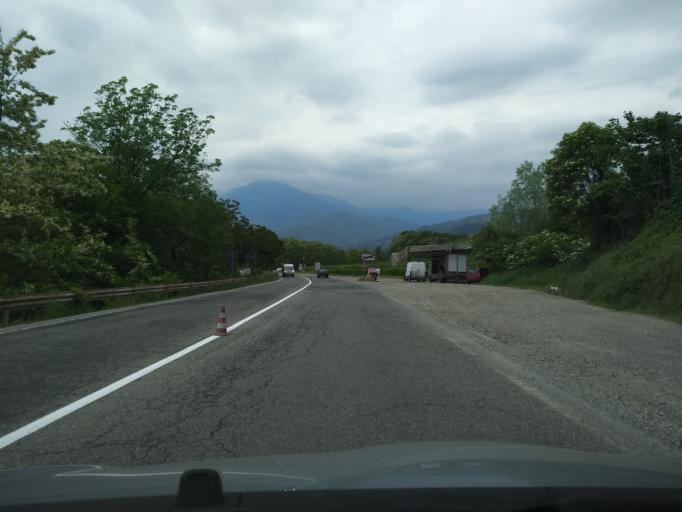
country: IT
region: Piedmont
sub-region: Provincia di Torino
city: Bibiana
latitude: 44.8097
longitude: 7.2846
